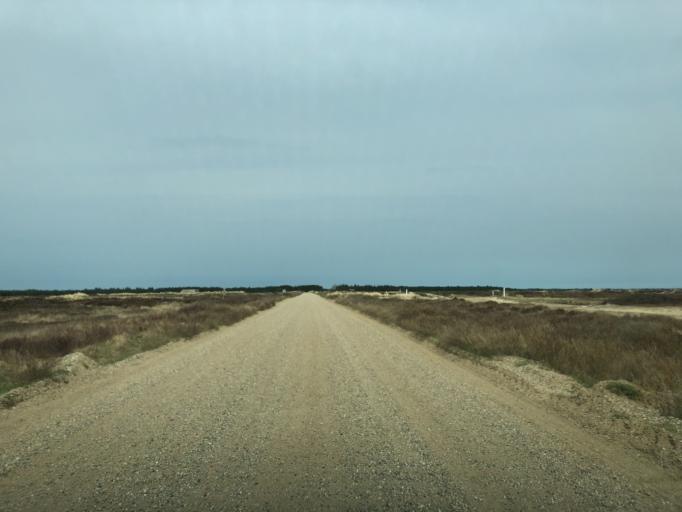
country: DK
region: South Denmark
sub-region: Varde Kommune
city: Oksbol
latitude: 55.5932
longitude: 8.1514
